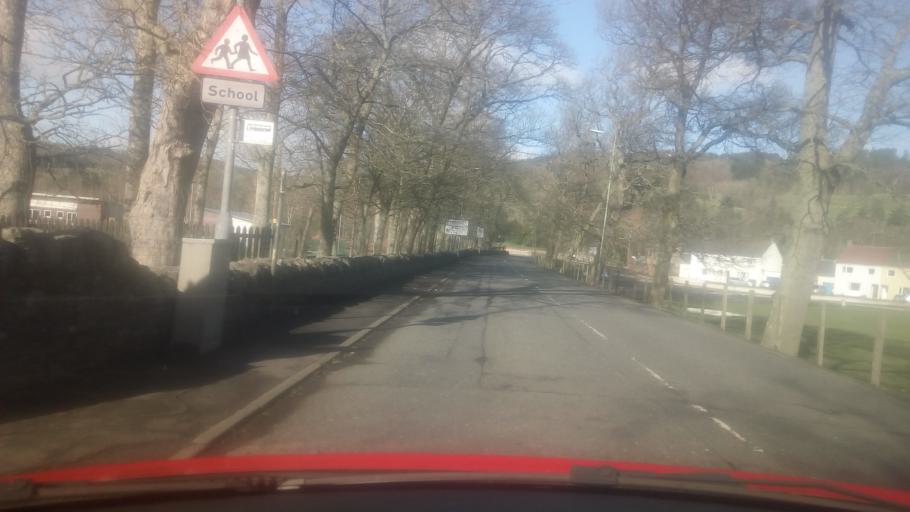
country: GB
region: Scotland
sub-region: The Scottish Borders
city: Selkirk
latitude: 55.5478
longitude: -2.8552
